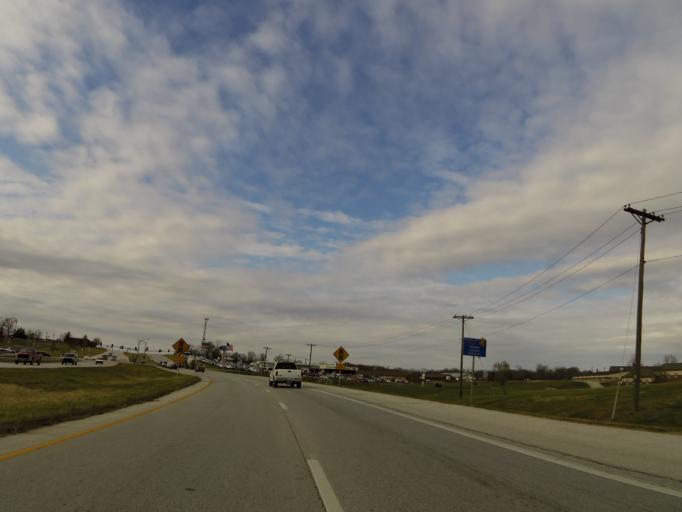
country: US
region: Missouri
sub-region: Marion County
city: Hannibal
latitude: 39.7279
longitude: -91.3932
